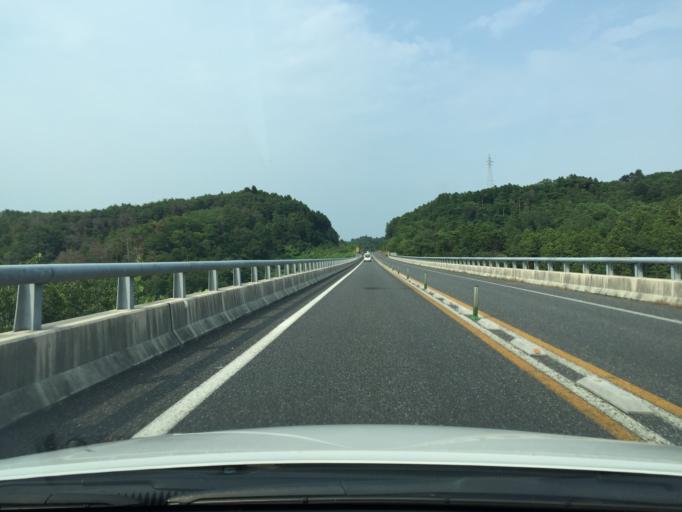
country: JP
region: Fukushima
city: Iwaki
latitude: 37.1314
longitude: 140.9512
